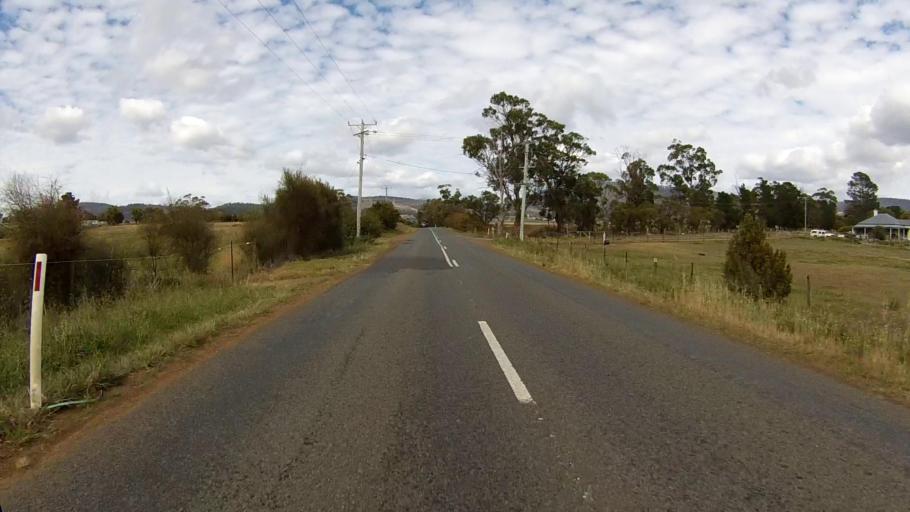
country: AU
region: Tasmania
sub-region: Clarence
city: Cambridge
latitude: -42.7464
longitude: 147.4157
